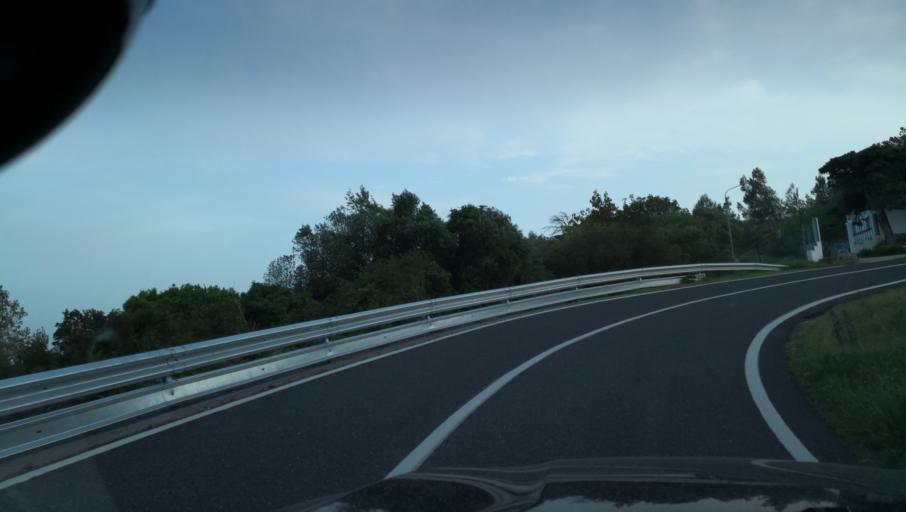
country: PT
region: Setubal
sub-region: Setubal
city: Setubal
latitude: 38.4913
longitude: -8.9372
